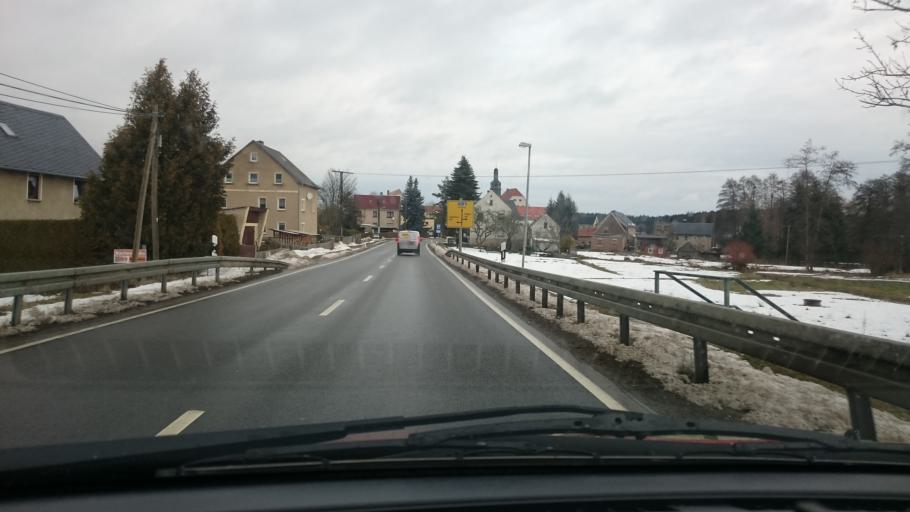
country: DE
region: Saxony
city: Waldkirchen
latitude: 50.6107
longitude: 12.4243
